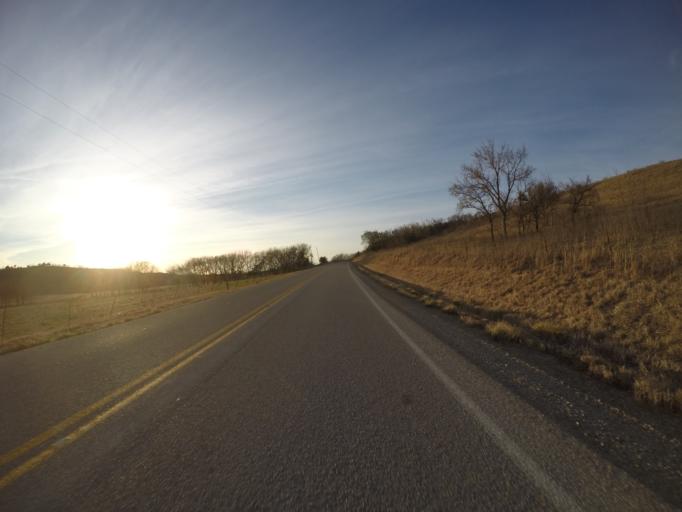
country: US
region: Kansas
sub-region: Riley County
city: Manhattan
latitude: 39.3015
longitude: -96.7081
